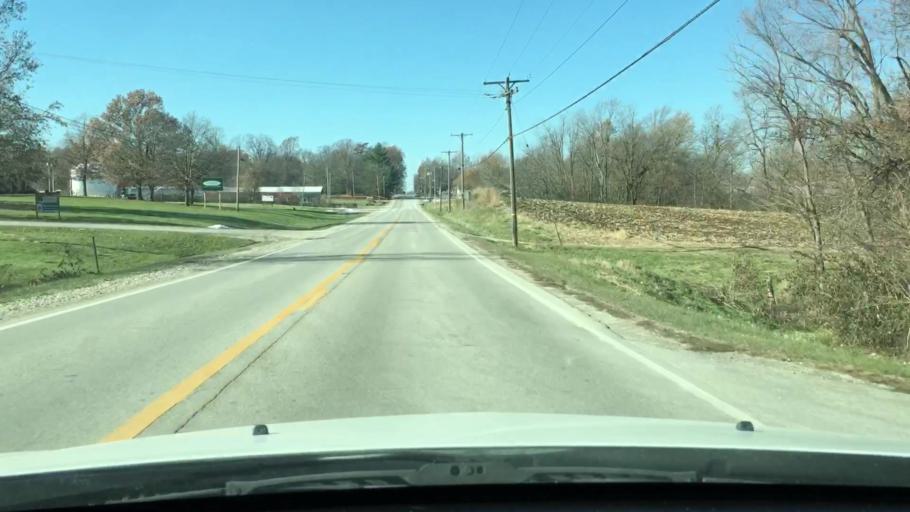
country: US
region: Illinois
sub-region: Pike County
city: Pittsfield
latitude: 39.6067
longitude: -90.7870
